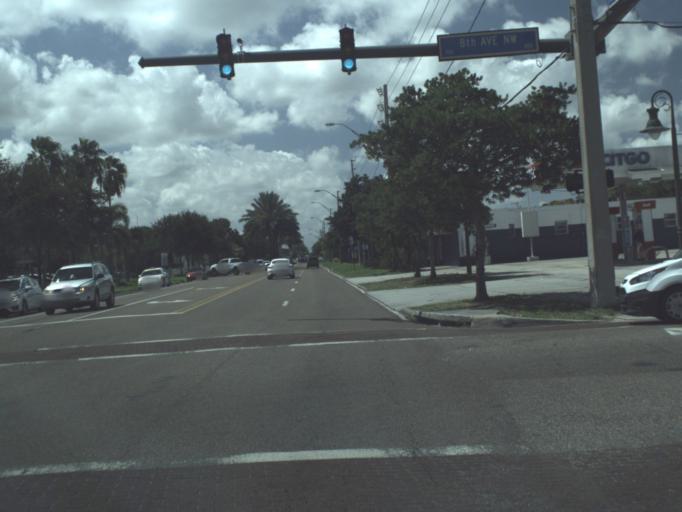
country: US
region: Florida
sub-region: Pinellas County
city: Belleair
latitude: 27.9242
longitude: -82.7964
